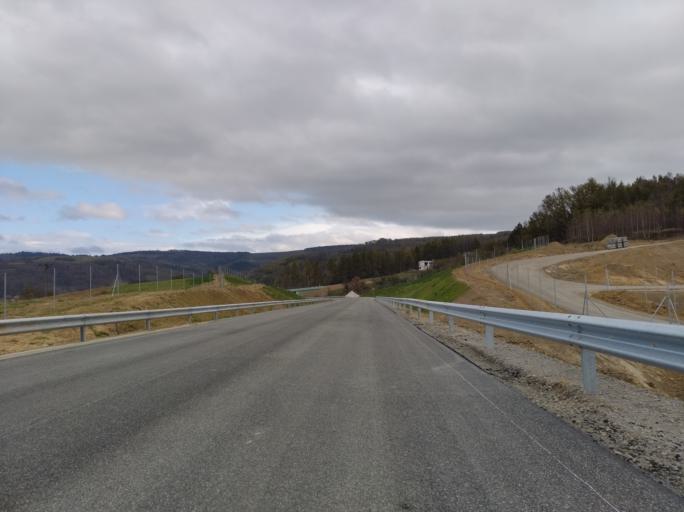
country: PL
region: Subcarpathian Voivodeship
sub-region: Powiat strzyzowski
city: Strzyzow
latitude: 49.8618
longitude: 21.8074
